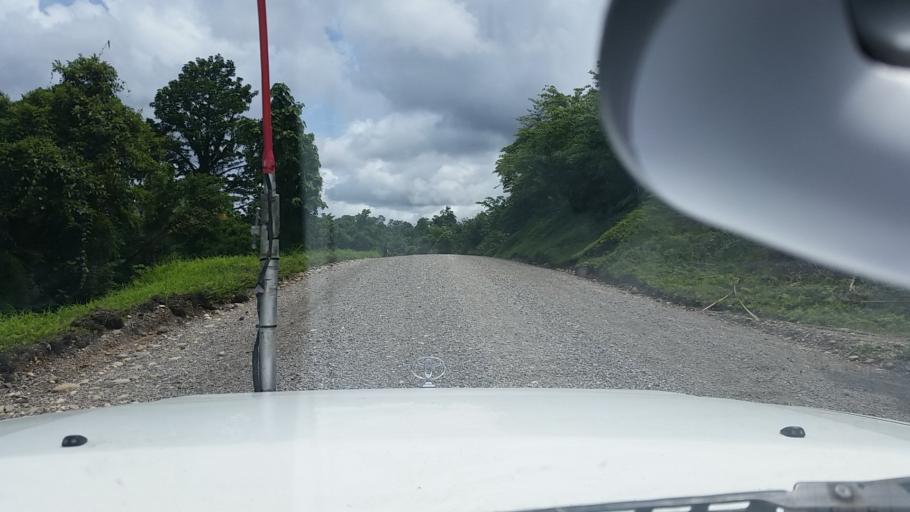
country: PG
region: Western Province
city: Kiunga
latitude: -5.6660
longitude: 141.1587
